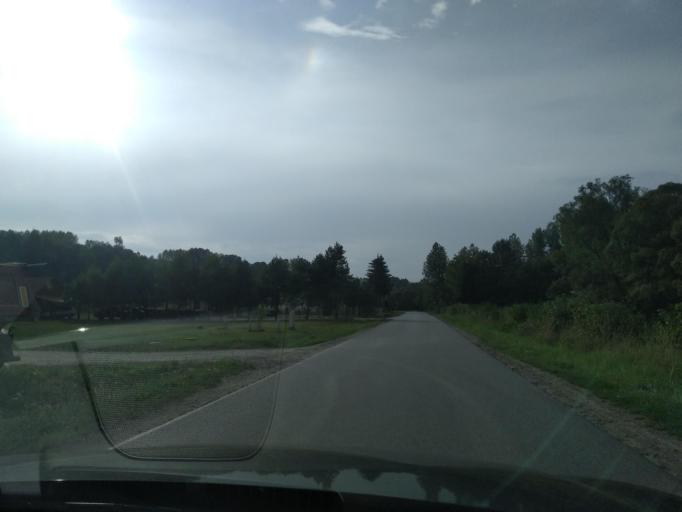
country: PL
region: Subcarpathian Voivodeship
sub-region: Powiat sanocki
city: Tyrawa Woloska
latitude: 49.5705
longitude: 22.3770
